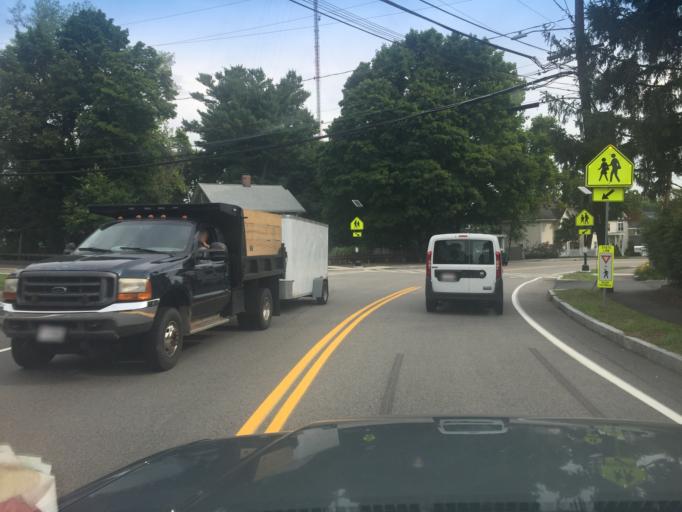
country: US
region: Massachusetts
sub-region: Norfolk County
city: Needham
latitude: 42.3061
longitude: -71.2383
